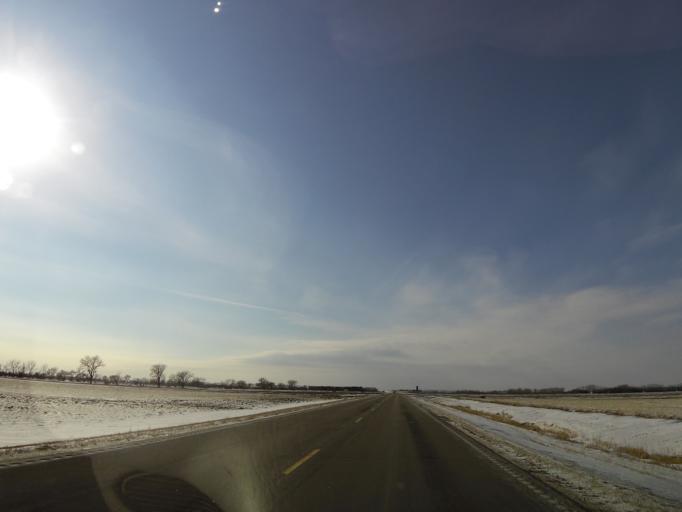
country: US
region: North Dakota
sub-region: Walsh County
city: Grafton
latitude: 48.4122
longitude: -97.1648
